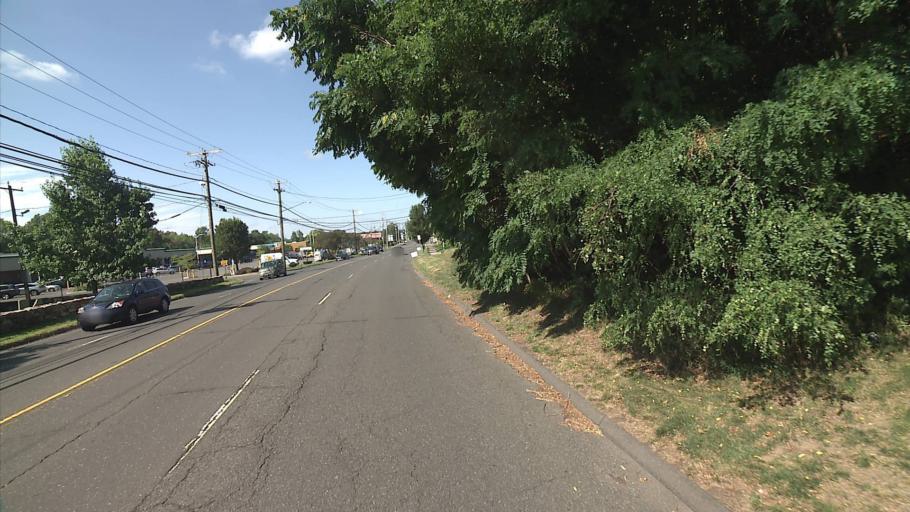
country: US
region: Connecticut
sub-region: Fairfield County
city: Westport
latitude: 41.1293
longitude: -73.3794
